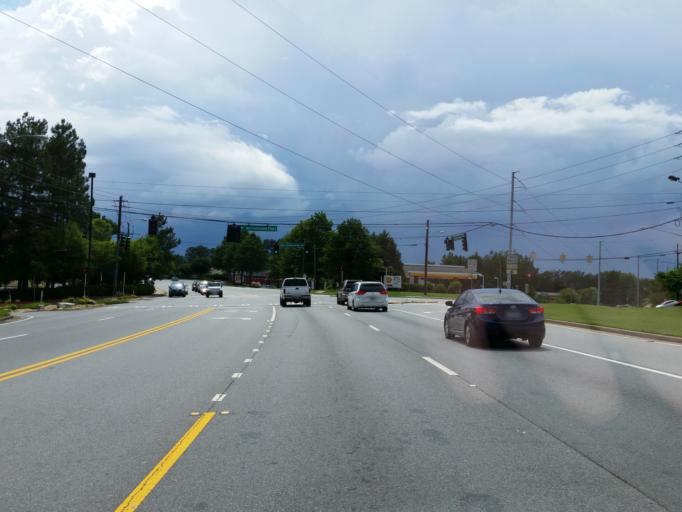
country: US
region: Georgia
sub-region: Fulton County
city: Alpharetta
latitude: 34.0662
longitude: -84.3175
